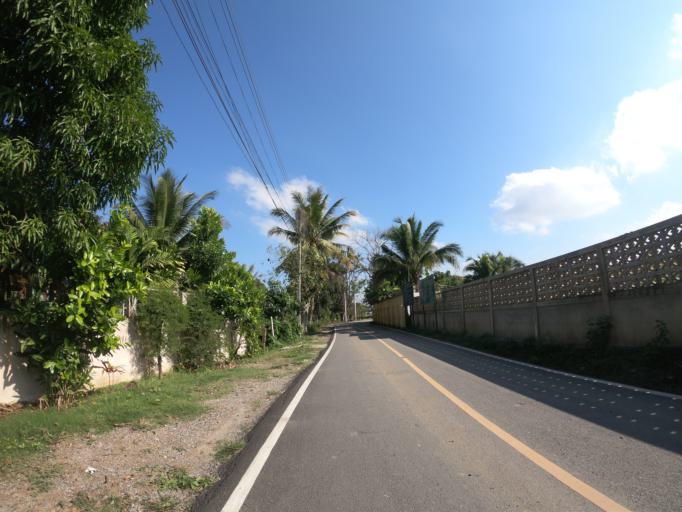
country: TH
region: Chiang Mai
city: Saraphi
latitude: 18.7166
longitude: 99.0050
